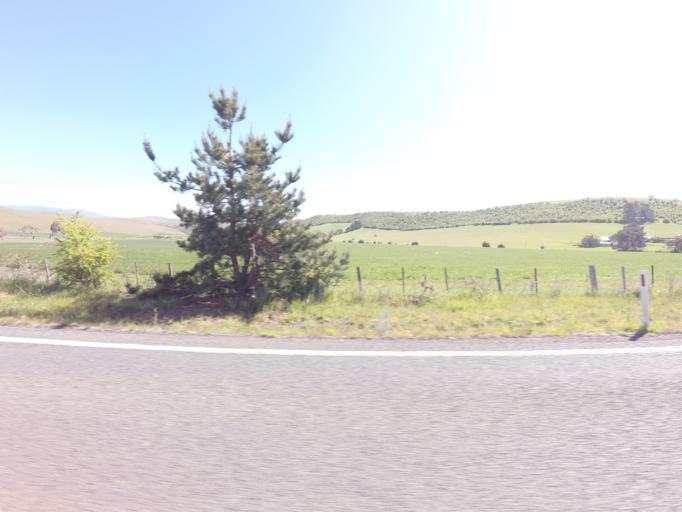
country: AU
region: Tasmania
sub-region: Derwent Valley
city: New Norfolk
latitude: -42.5669
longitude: 146.8809
